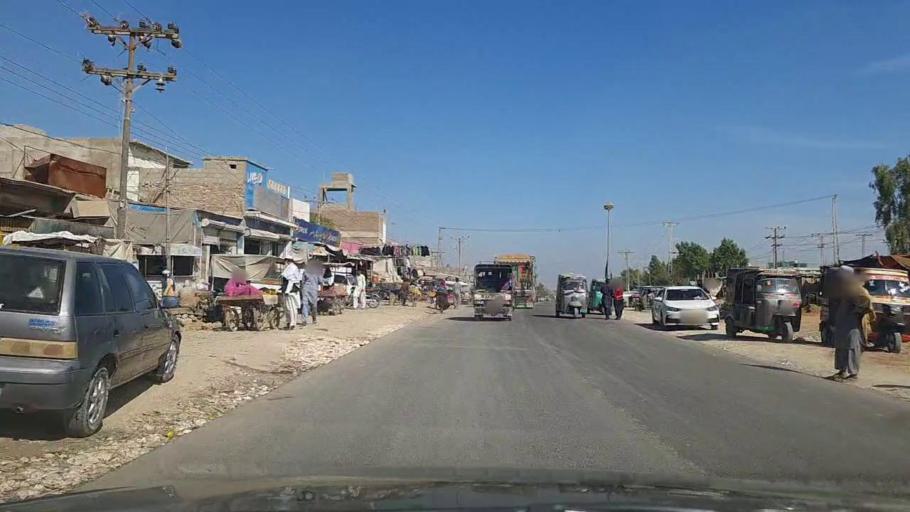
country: PK
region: Sindh
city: Kotri
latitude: 25.3494
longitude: 68.2647
